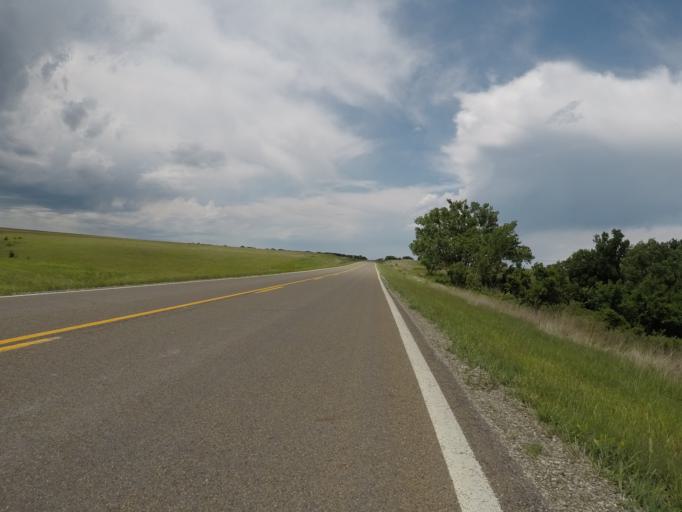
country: US
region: Kansas
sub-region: Wabaunsee County
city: Alma
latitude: 38.8551
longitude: -96.3786
